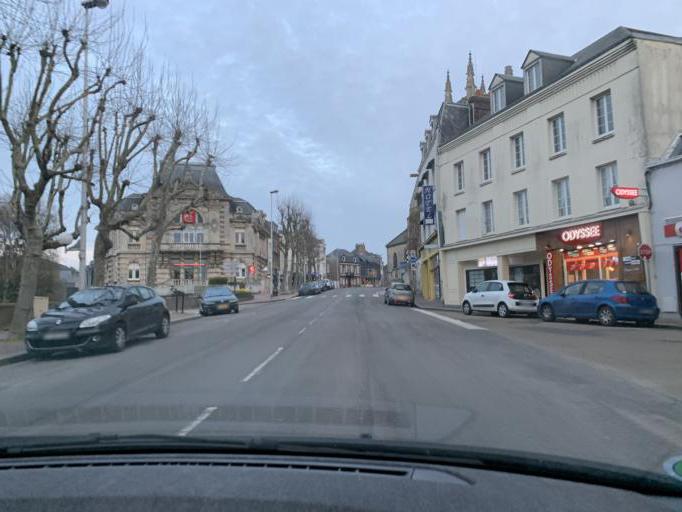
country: FR
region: Haute-Normandie
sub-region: Departement de la Seine-Maritime
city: Fecamp
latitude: 49.7588
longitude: 0.3751
